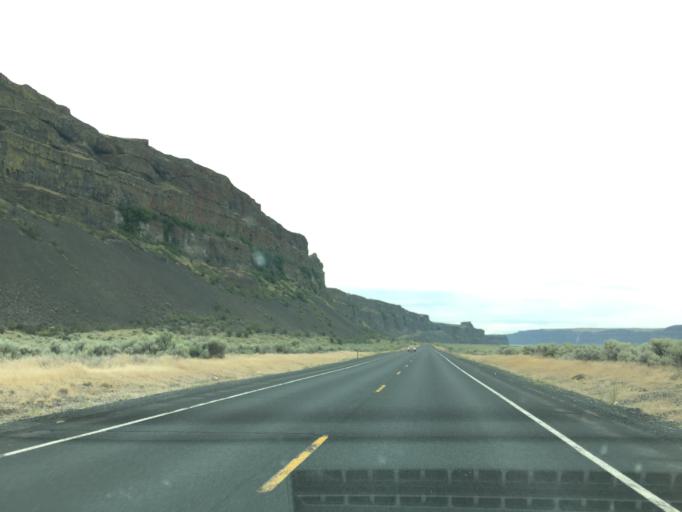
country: US
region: Washington
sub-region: Okanogan County
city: Coulee Dam
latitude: 47.7656
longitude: -119.2122
